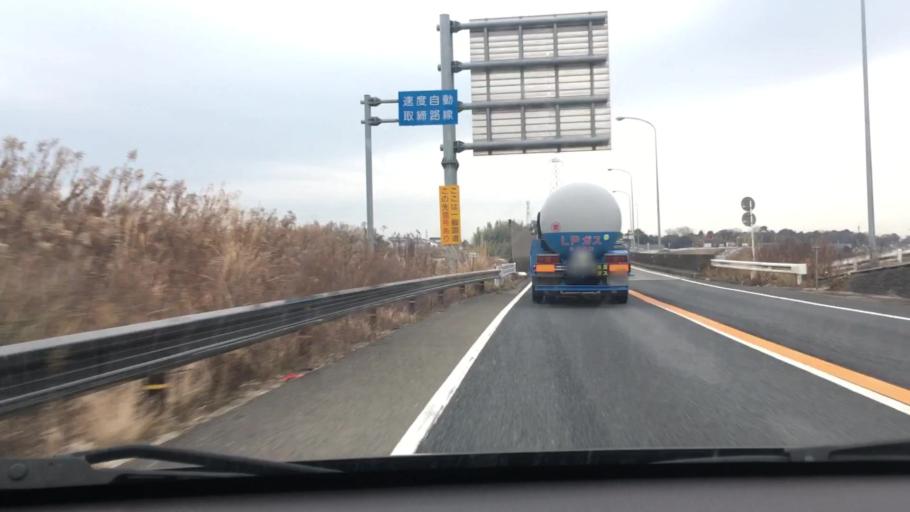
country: JP
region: Mie
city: Kameyama
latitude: 34.8630
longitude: 136.4366
